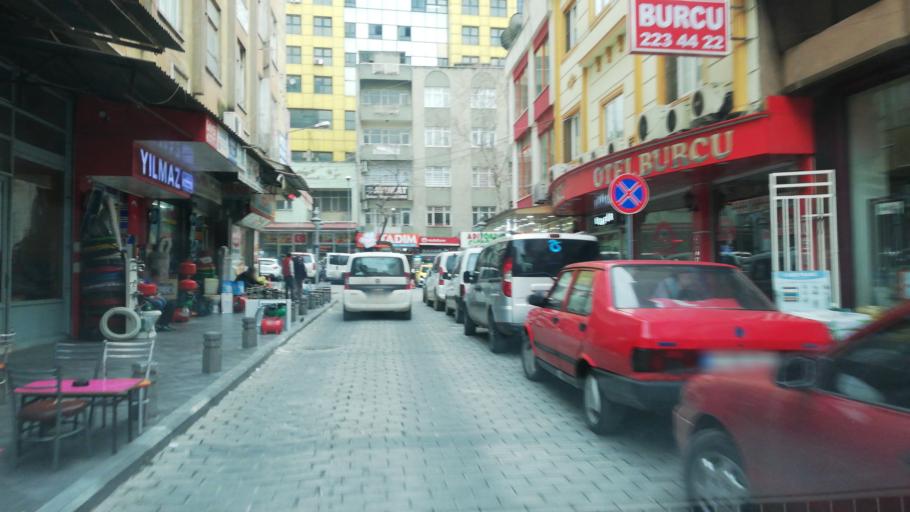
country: TR
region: Kahramanmaras
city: Kahramanmaras
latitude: 37.5811
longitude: 36.9284
